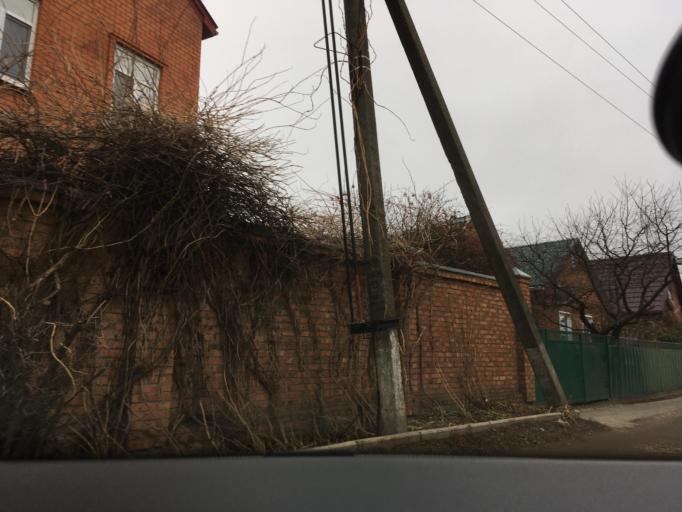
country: RU
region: Krasnodarskiy
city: Kushchevskaya
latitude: 46.5769
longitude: 39.6212
